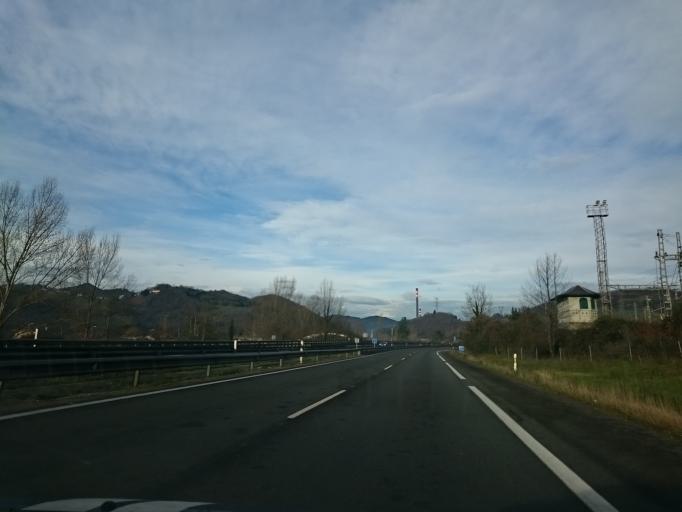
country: ES
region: Asturias
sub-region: Province of Asturias
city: Castandiello
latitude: 43.3075
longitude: -5.8585
